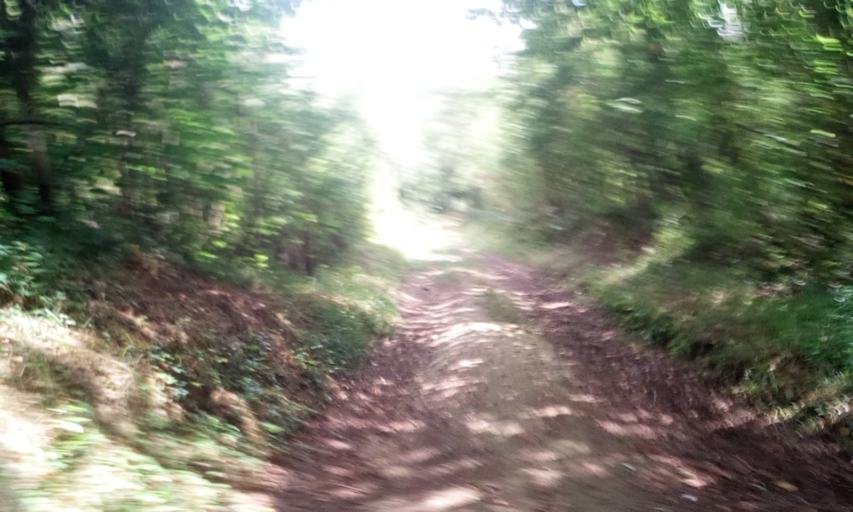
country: FR
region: Lower Normandy
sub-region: Departement du Calvados
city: Cagny
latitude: 49.1133
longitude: -0.2529
